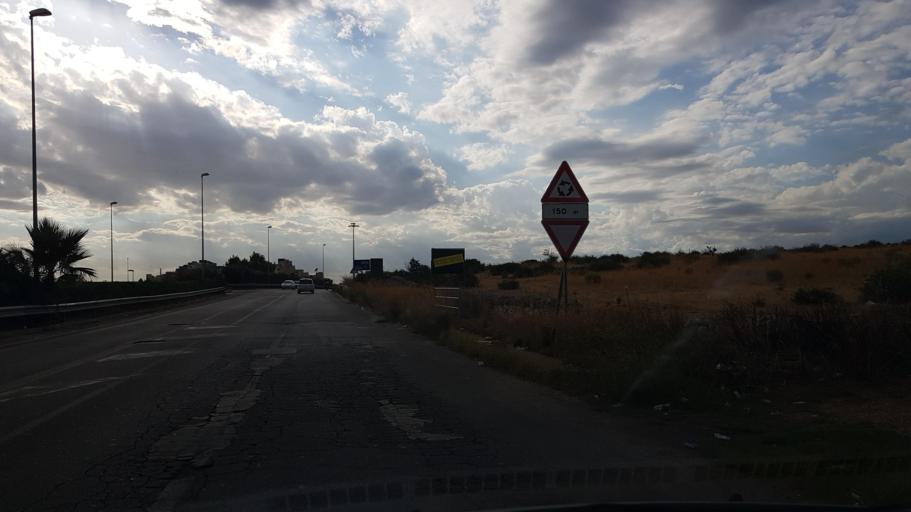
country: IT
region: Apulia
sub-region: Provincia di Taranto
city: Paolo VI
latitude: 40.5187
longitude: 17.2901
